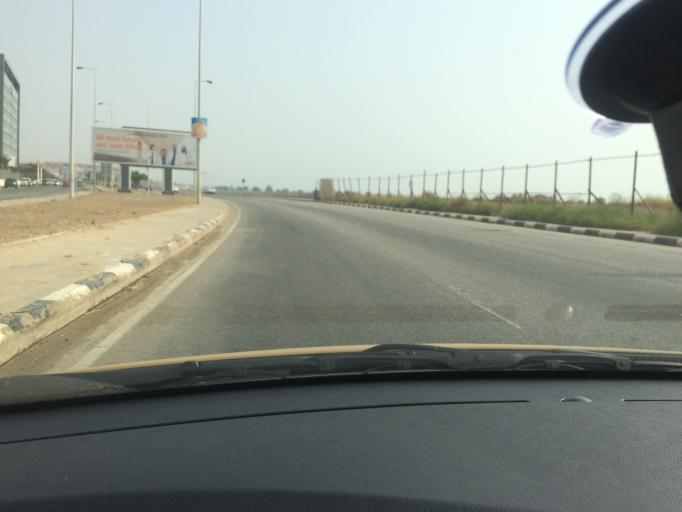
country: AO
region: Luanda
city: Luanda
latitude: -8.8174
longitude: 13.2172
